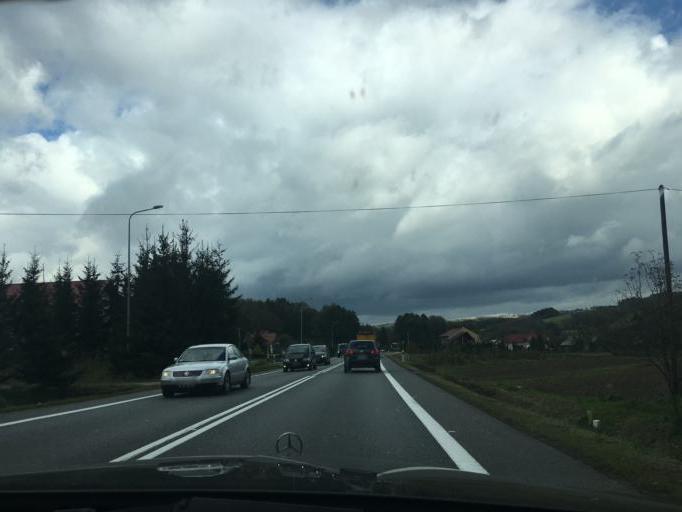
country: PL
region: Subcarpathian Voivodeship
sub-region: Powiat strzyzowski
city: Niebylec
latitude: 49.8669
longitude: 21.9023
